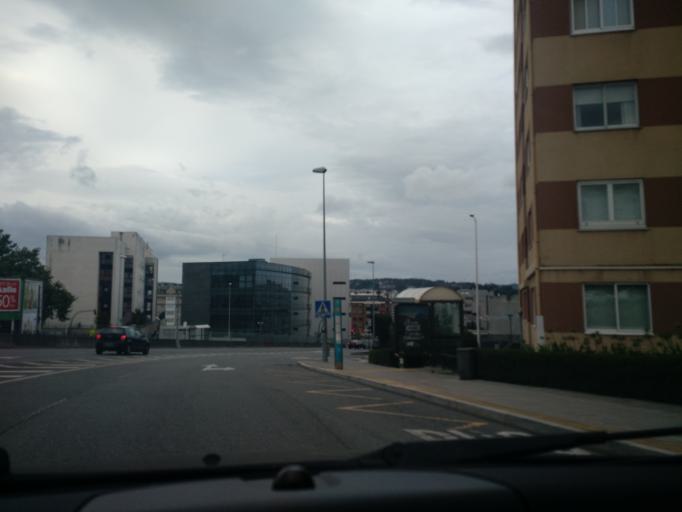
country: ES
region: Galicia
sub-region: Provincia da Coruna
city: A Coruna
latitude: 43.3431
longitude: -8.4001
